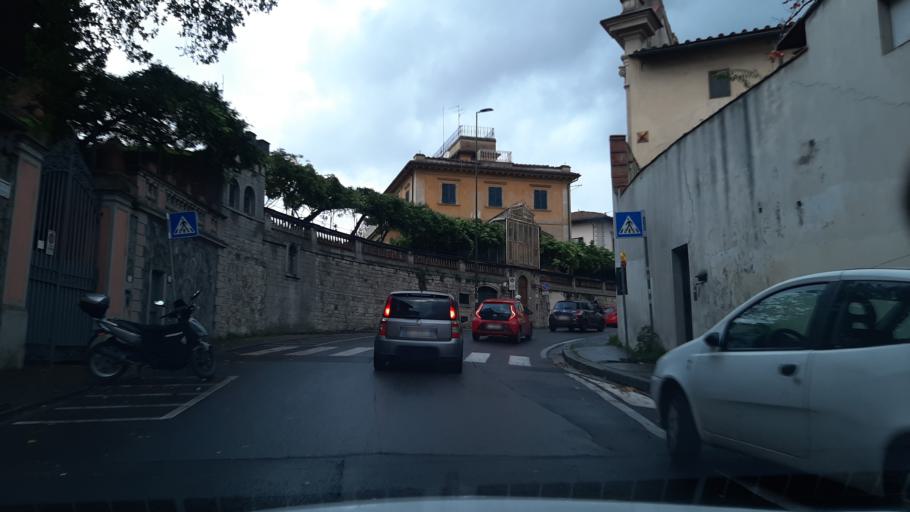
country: IT
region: Tuscany
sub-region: Province of Florence
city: Florence
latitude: 43.7903
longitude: 11.2619
